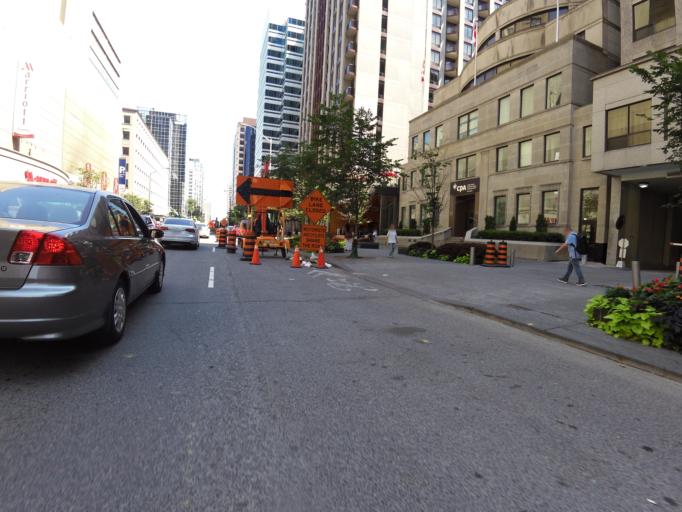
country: CA
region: Ontario
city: Toronto
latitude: 43.6707
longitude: -79.3853
